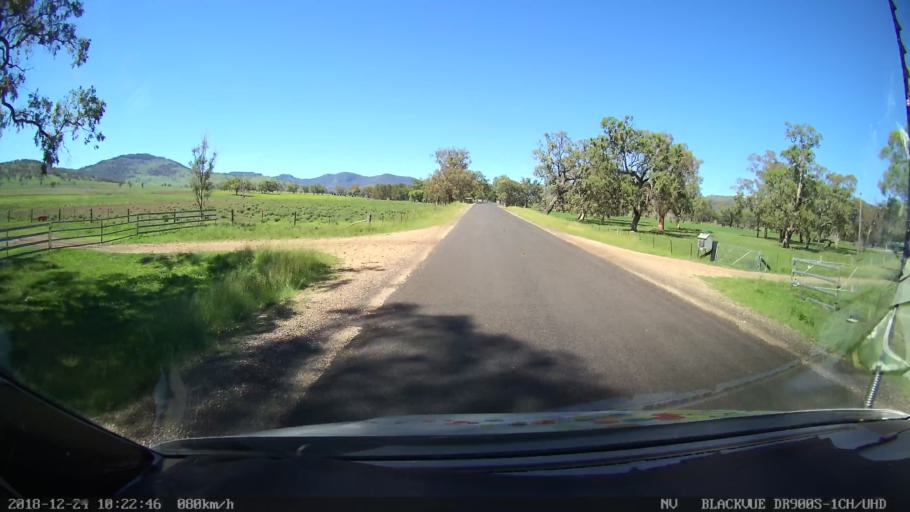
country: AU
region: New South Wales
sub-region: Liverpool Plains
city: Quirindi
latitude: -31.7681
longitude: 150.5424
